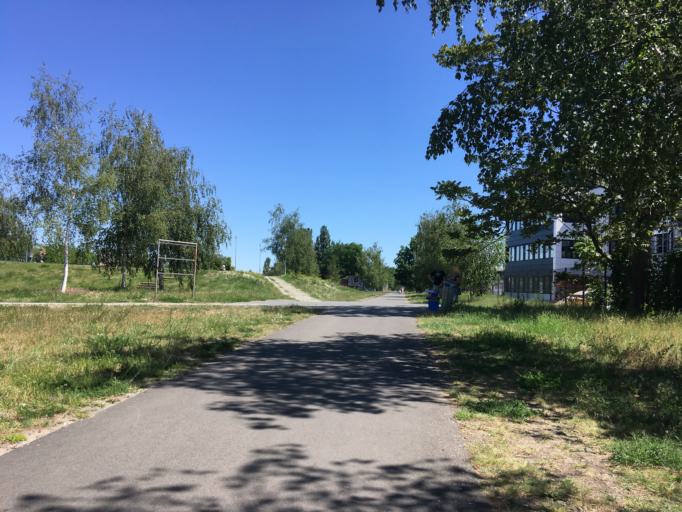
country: DE
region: Berlin
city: Johannisthal
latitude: 52.4412
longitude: 13.5079
